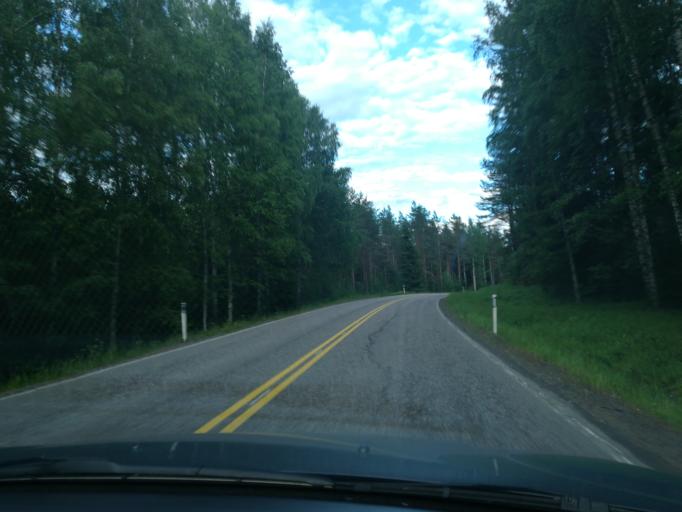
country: FI
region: Southern Savonia
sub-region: Mikkeli
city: Puumala
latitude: 61.5192
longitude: 27.8969
